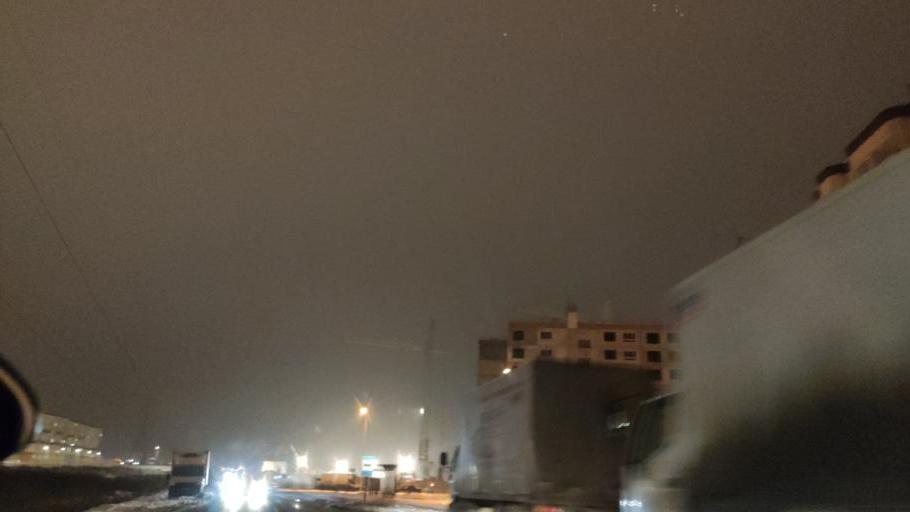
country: RU
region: Moscow
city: Zagor'ye
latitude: 55.5352
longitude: 37.6372
